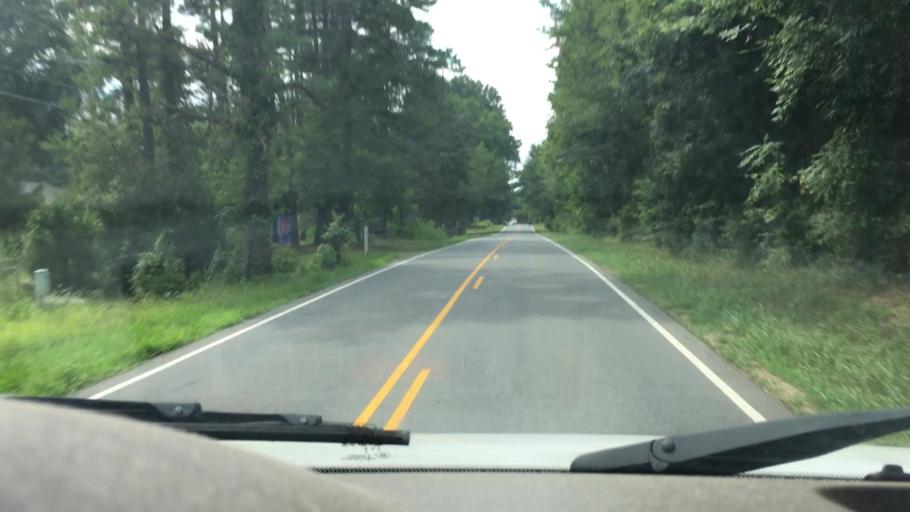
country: US
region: North Carolina
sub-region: Gaston County
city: Davidson
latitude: 35.4810
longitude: -80.8064
